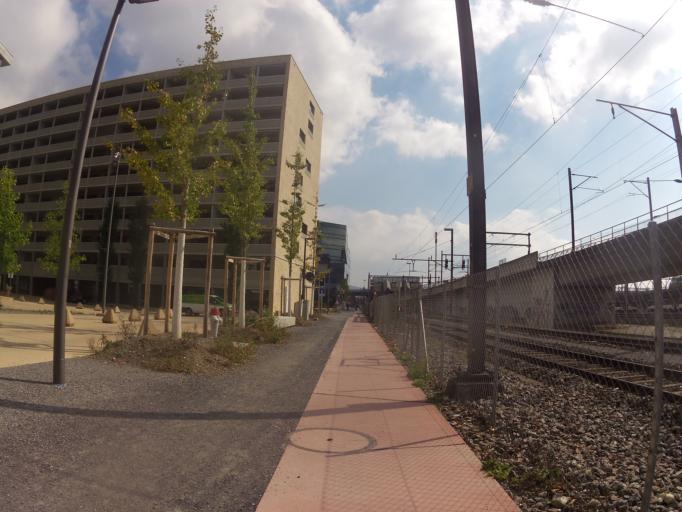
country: CH
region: Zurich
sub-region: Bezirk Zuerich
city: Zuerich (Kreis 5) / Escher-Wyss
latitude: 47.3864
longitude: 8.5136
